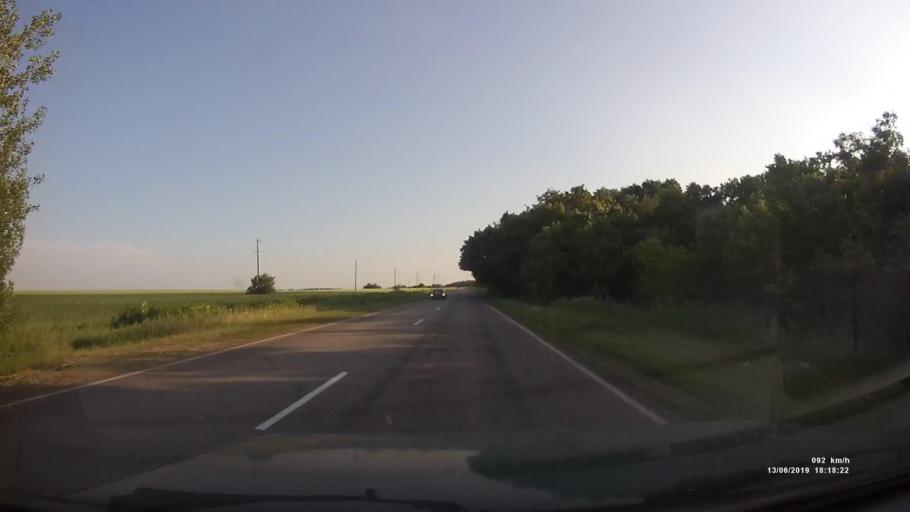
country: RU
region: Rostov
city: Kazanskaya
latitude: 49.9089
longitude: 41.3148
